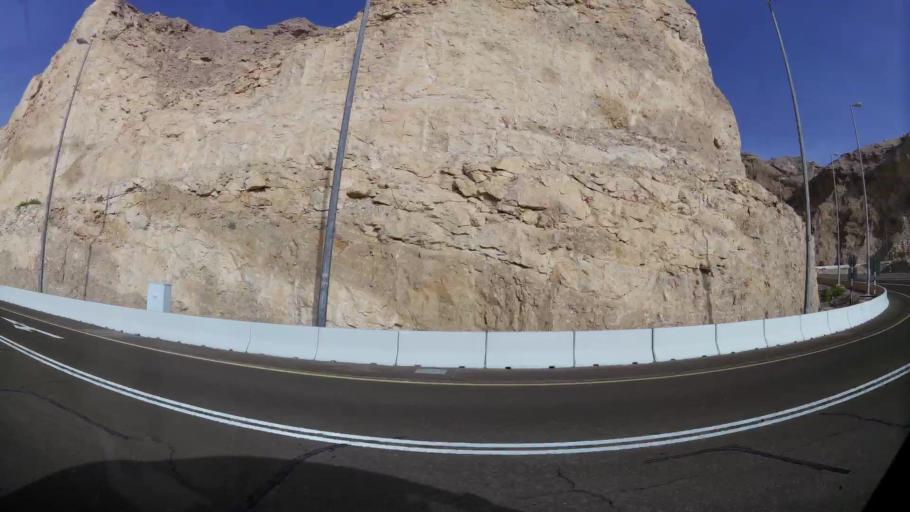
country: AE
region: Abu Dhabi
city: Al Ain
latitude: 24.0974
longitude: 55.7583
